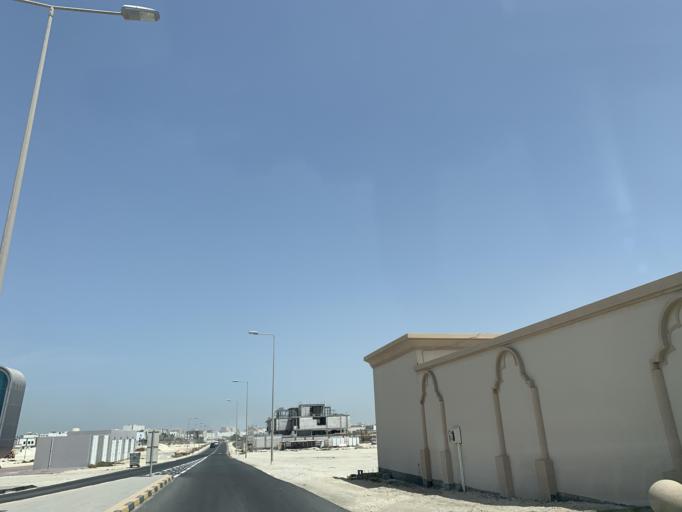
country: BH
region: Northern
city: Madinat `Isa
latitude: 26.1508
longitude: 50.5446
